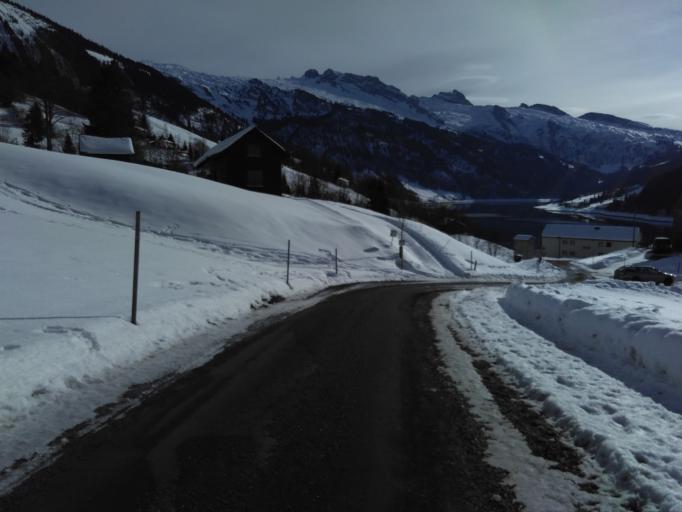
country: CH
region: Schwyz
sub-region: Bezirk March
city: Vorderthal
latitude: 47.1081
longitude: 8.9210
